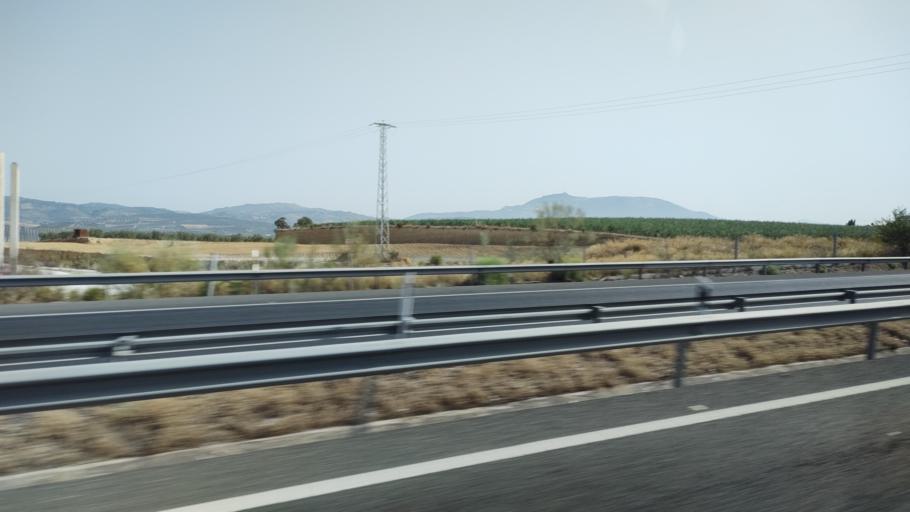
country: ES
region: Andalusia
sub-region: Provincia de Granada
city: Villanueva de Mesia
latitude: 37.1954
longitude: -4.0180
